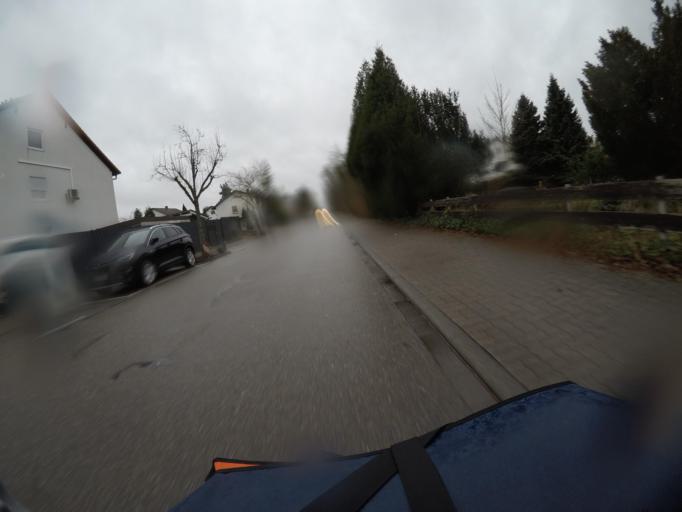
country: DE
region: Baden-Wuerttemberg
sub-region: Karlsruhe Region
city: Linkenheim-Hochstetten
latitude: 49.1038
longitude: 8.4720
